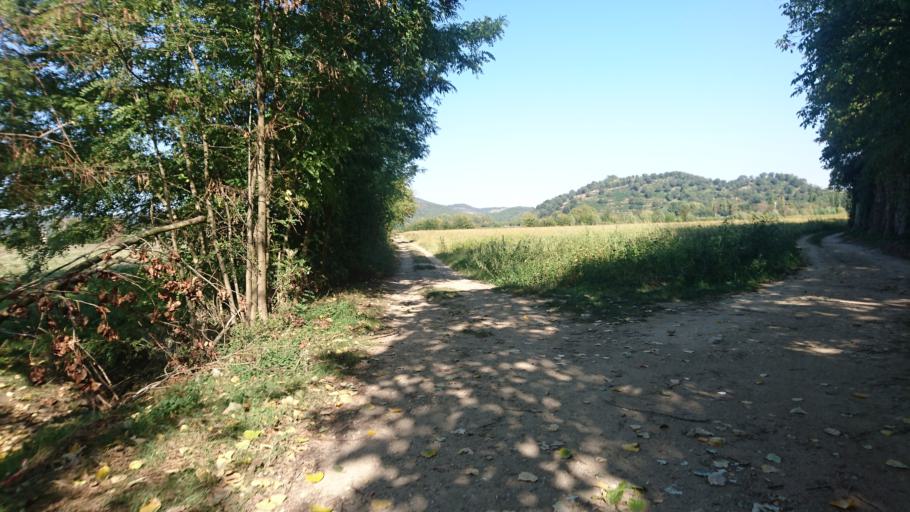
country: IT
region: Veneto
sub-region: Provincia di Padova
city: Battaglia Terme
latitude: 45.2771
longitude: 11.7535
